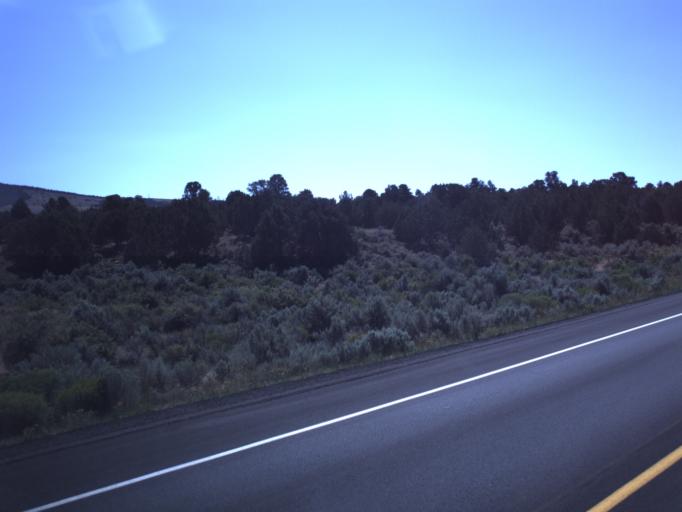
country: US
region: Utah
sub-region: Utah County
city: Eagle Mountain
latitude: 40.0087
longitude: -112.2763
